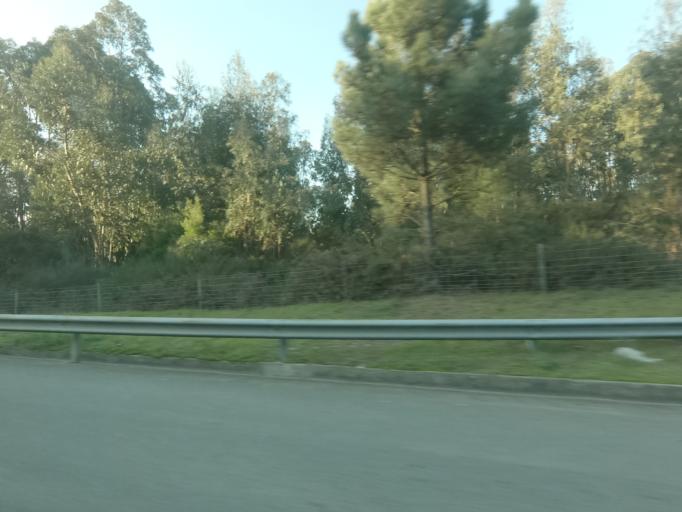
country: PT
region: Porto
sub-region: Penafiel
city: Penafiel
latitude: 41.2184
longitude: -8.2676
